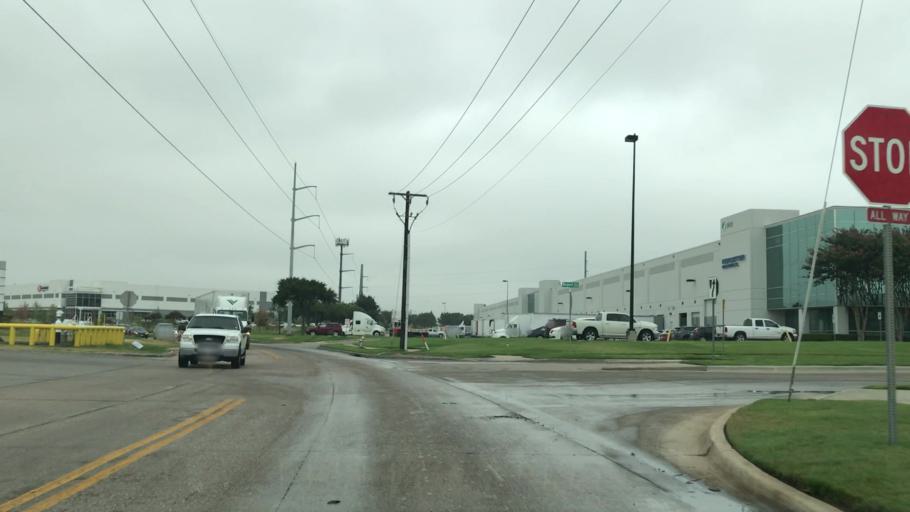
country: US
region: Texas
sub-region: Dallas County
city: Coppell
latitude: 32.9398
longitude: -97.0197
